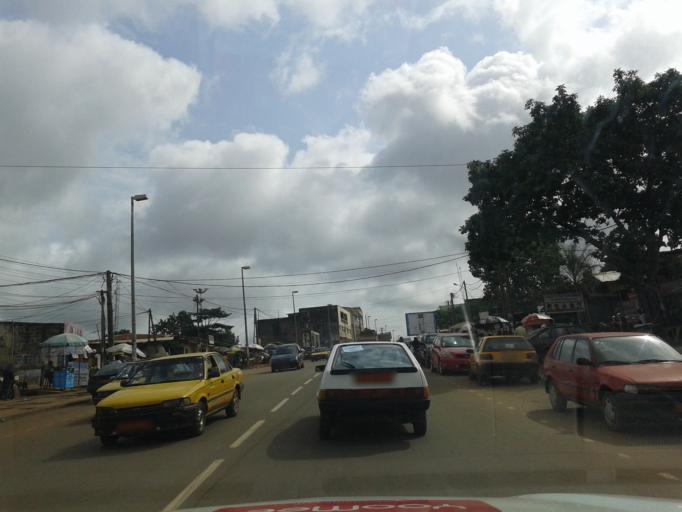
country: CM
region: Centre
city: Yaounde
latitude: 3.8843
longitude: 11.4970
